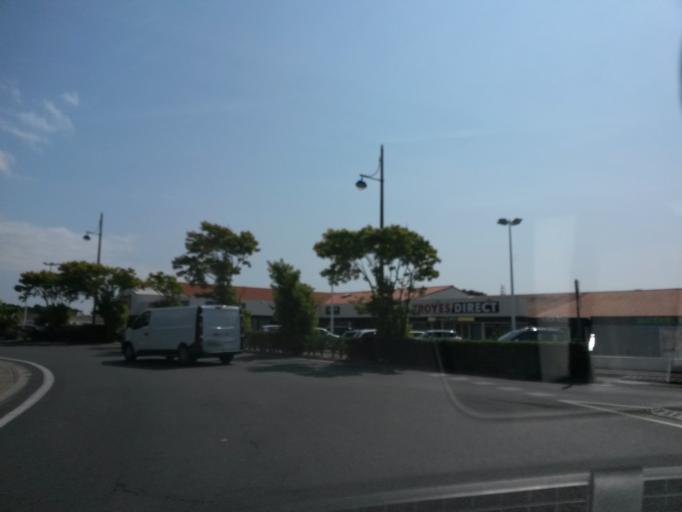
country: FR
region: Pays de la Loire
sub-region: Departement de la Vendee
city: La Tranche-sur-Mer
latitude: 46.3517
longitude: -1.4294
